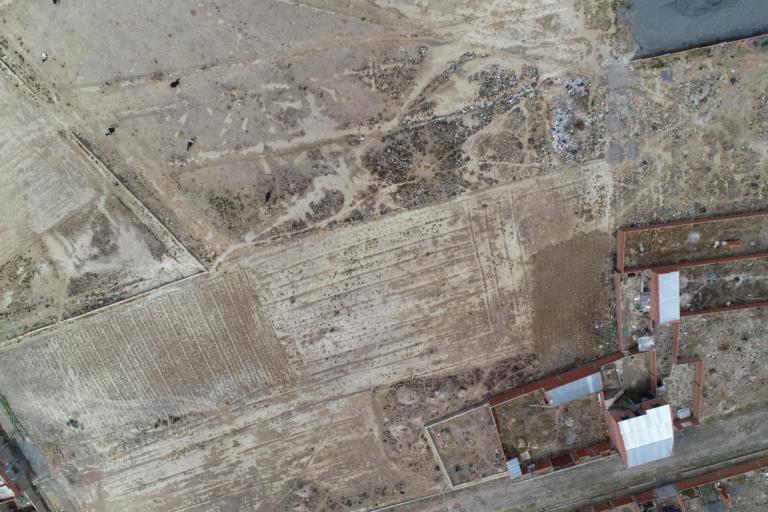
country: BO
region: La Paz
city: Achacachi
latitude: -16.0531
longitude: -68.6793
